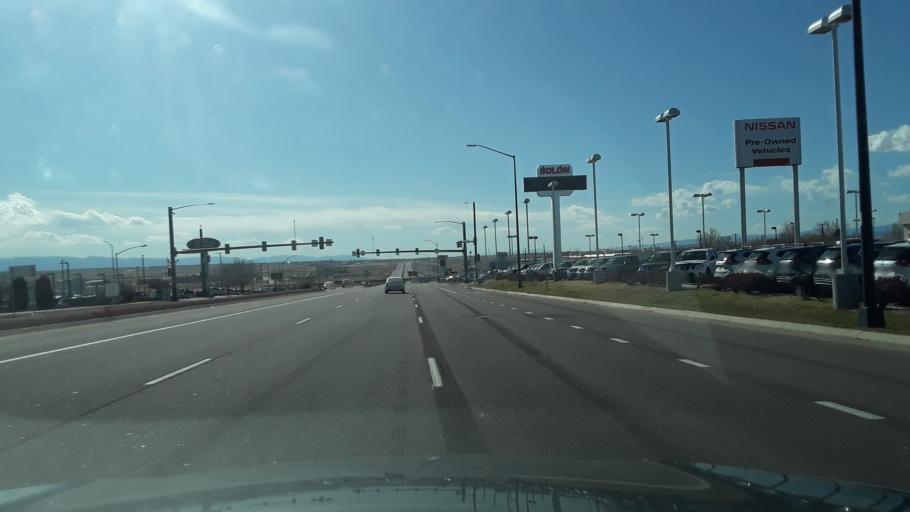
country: US
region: Colorado
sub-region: Pueblo County
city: Pueblo
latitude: 38.3111
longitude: -104.6404
